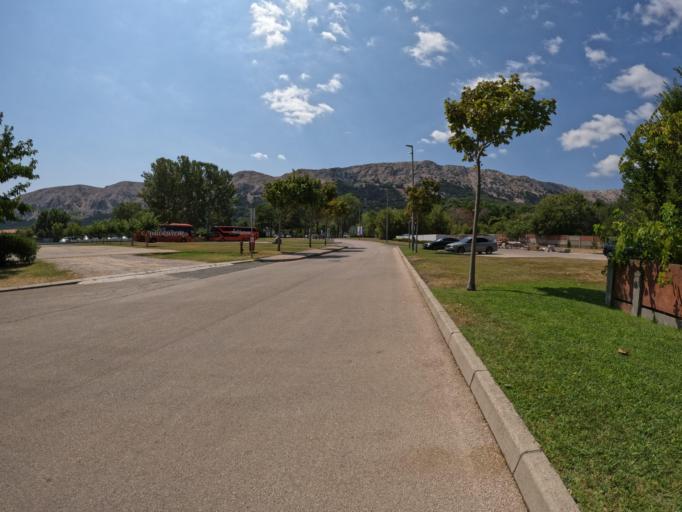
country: HR
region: Primorsko-Goranska
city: Punat
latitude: 44.9679
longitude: 14.7468
